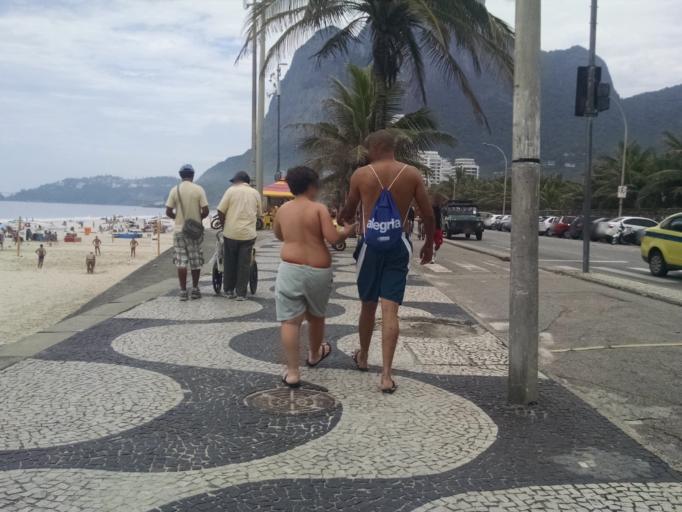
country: BR
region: Rio de Janeiro
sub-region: Rio De Janeiro
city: Rio de Janeiro
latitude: -22.9990
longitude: -43.2594
